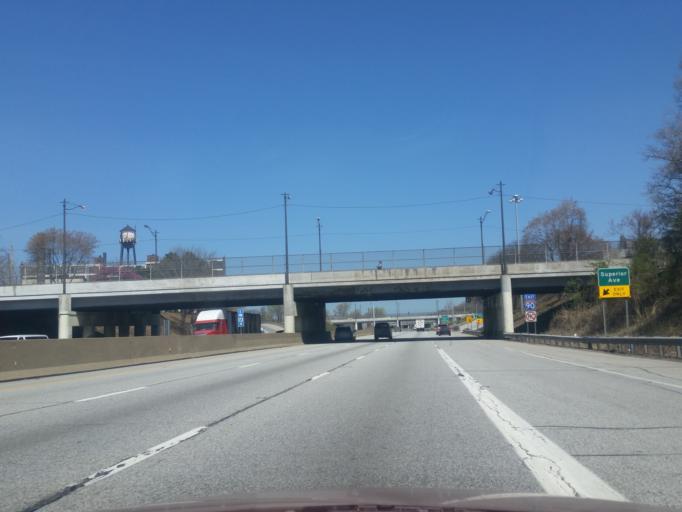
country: US
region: Ohio
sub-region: Cuyahoga County
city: Cleveland
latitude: 41.5065
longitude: -81.6708
